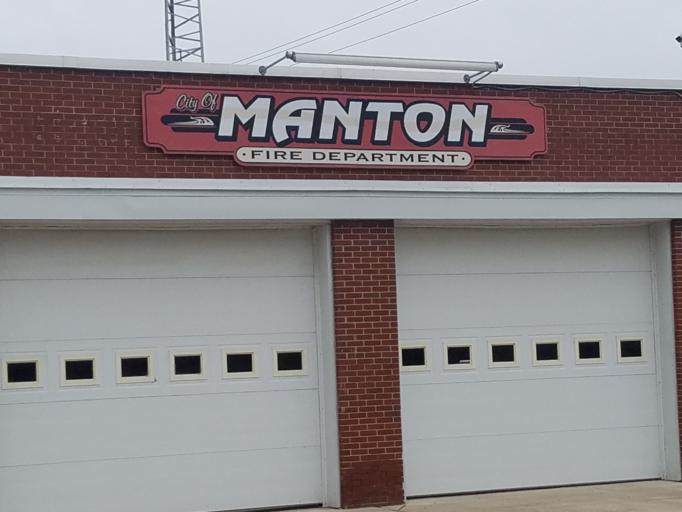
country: US
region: Michigan
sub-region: Wexford County
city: Manton
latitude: 44.4146
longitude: -85.3983
